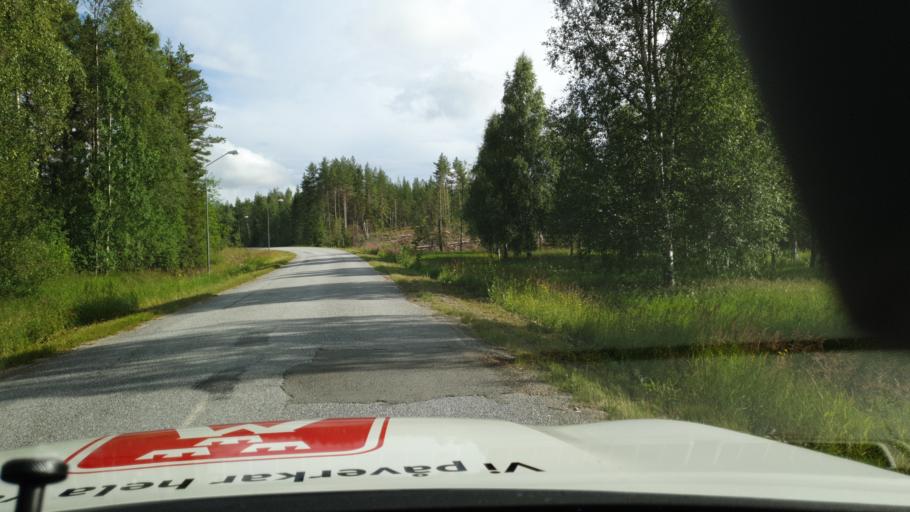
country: SE
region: Vaesterbotten
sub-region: Skelleftea Kommun
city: Burea
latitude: 64.4874
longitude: 21.0348
